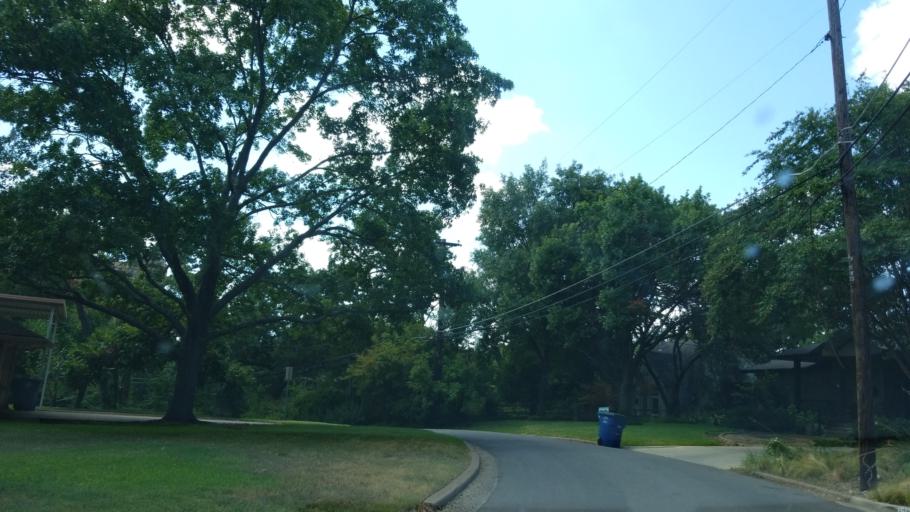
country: US
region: Texas
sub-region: Dallas County
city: Dallas
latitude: 32.7639
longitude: -96.8269
